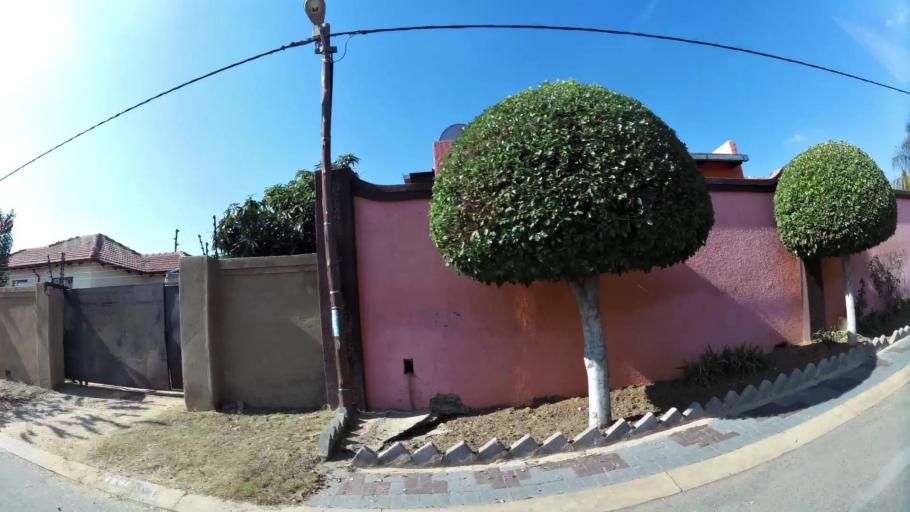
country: ZA
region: Gauteng
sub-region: West Rand District Municipality
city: Muldersdriseloop
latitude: -26.0230
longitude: 27.9332
